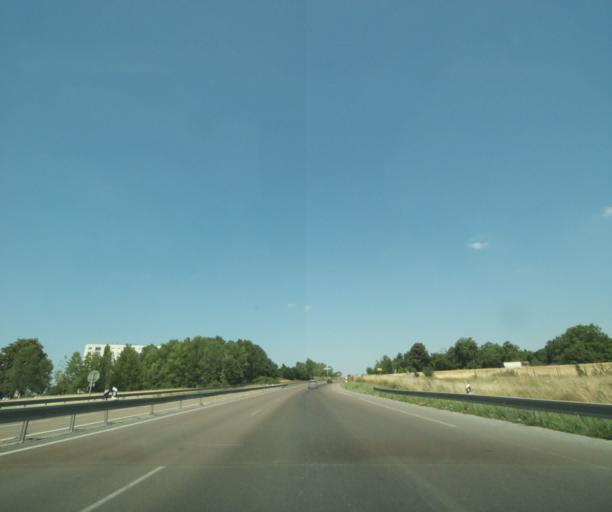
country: FR
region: Champagne-Ardenne
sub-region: Departement de la Marne
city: Saint-Memmie
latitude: 48.9653
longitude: 4.3866
